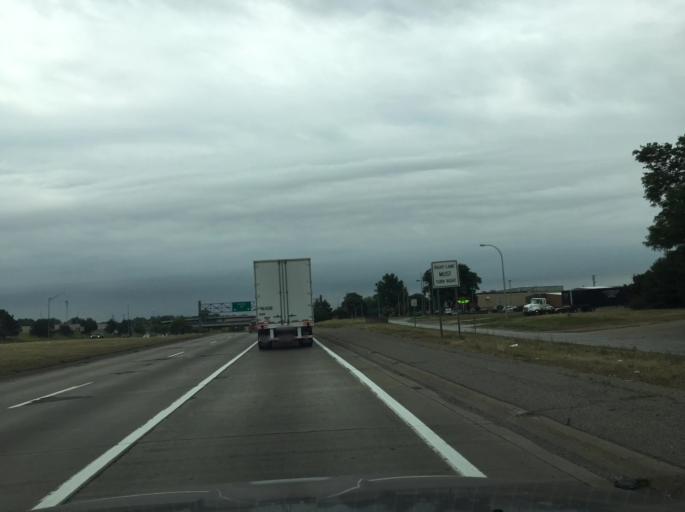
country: US
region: Michigan
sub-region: Macomb County
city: Center Line
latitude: 42.4960
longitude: -83.0464
